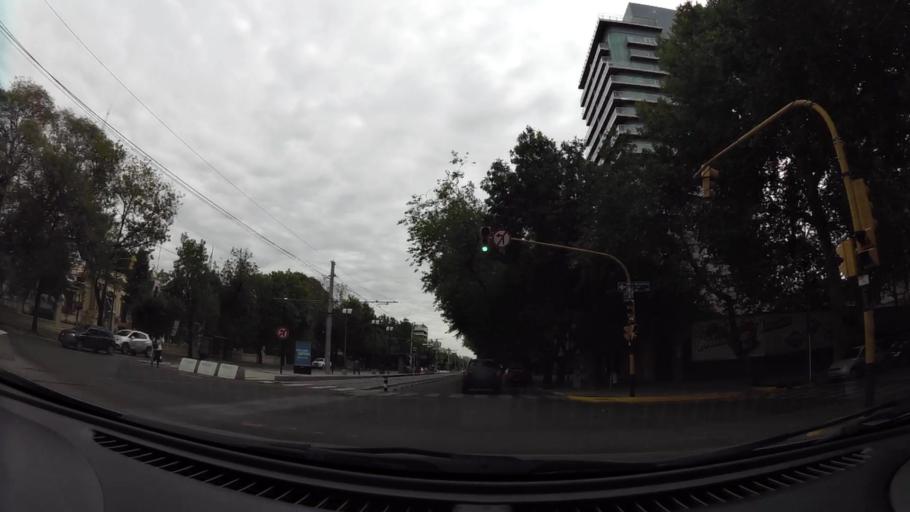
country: AR
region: Mendoza
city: Mendoza
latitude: -32.8909
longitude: -68.8503
